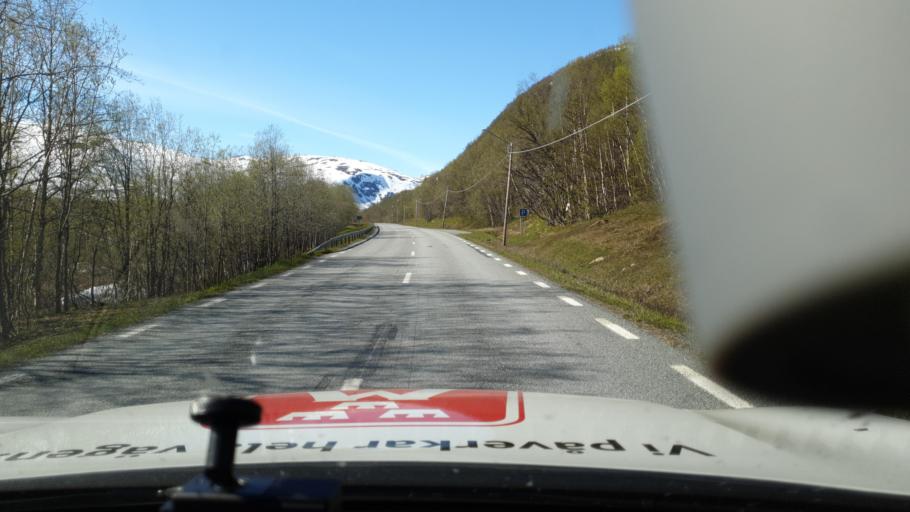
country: NO
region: Nordland
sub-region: Rana
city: Mo i Rana
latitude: 65.8701
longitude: 15.0136
